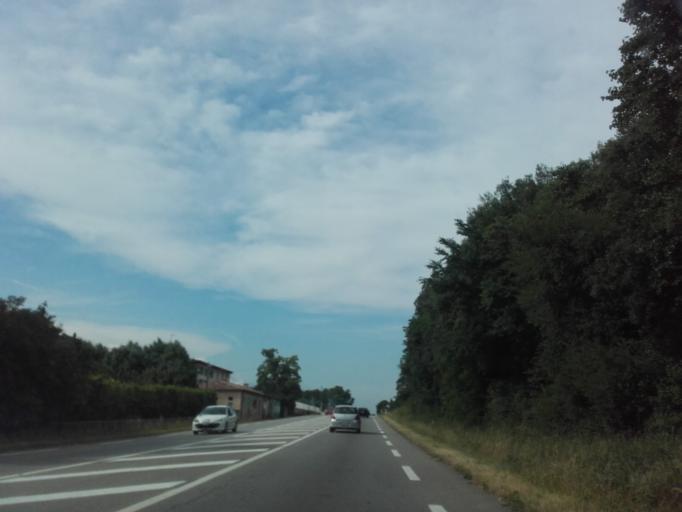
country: FR
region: Rhone-Alpes
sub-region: Departement de la Drome
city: Savasse
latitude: 44.5986
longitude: 4.7528
